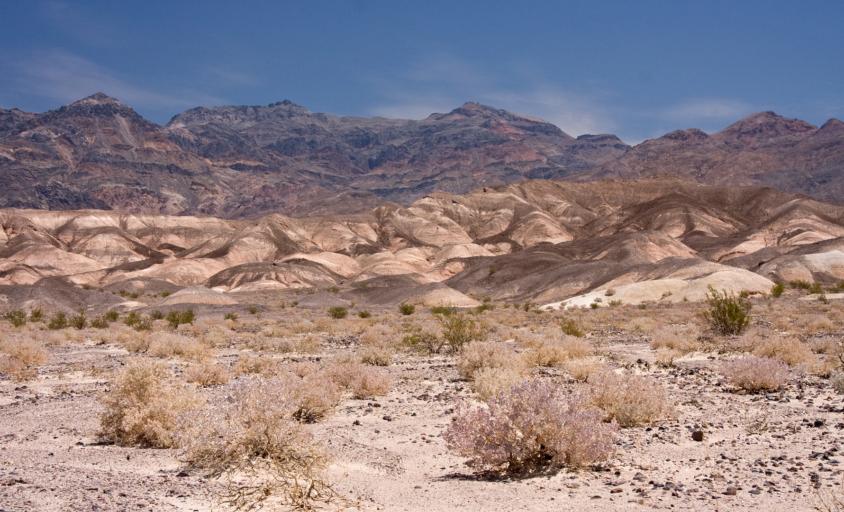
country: US
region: Nevada
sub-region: Nye County
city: Beatty
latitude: 36.6880
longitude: -117.0952
